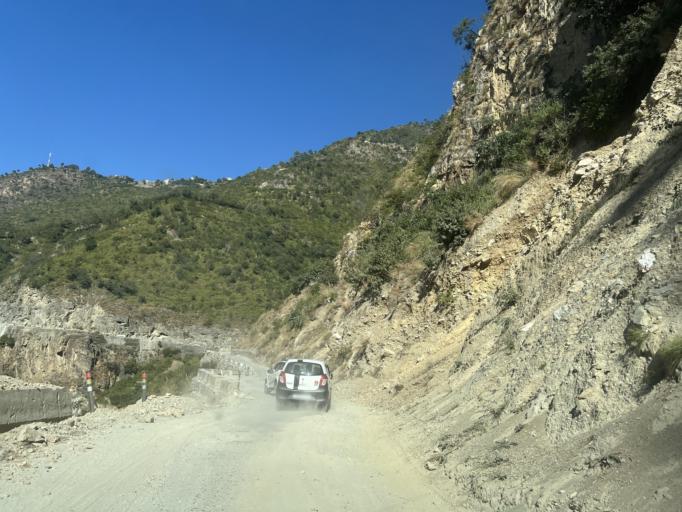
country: IN
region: Uttarakhand
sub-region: Naini Tal
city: Naini Tal
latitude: 29.5085
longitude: 79.4534
